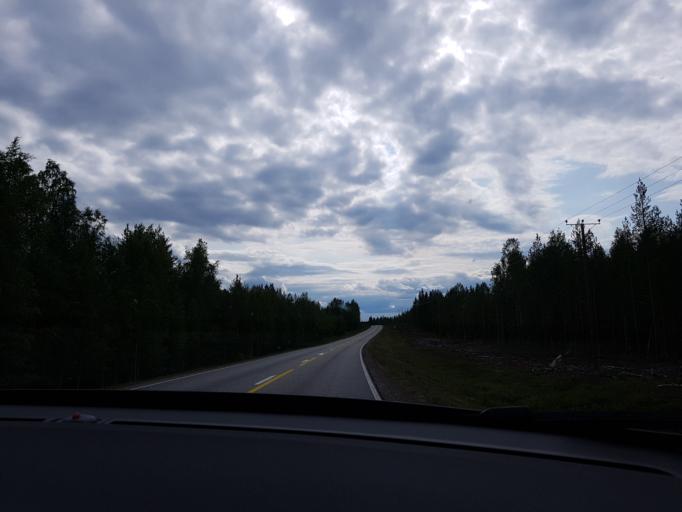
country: FI
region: Kainuu
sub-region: Kehys-Kainuu
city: Kuhmo
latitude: 64.3096
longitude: 29.8653
